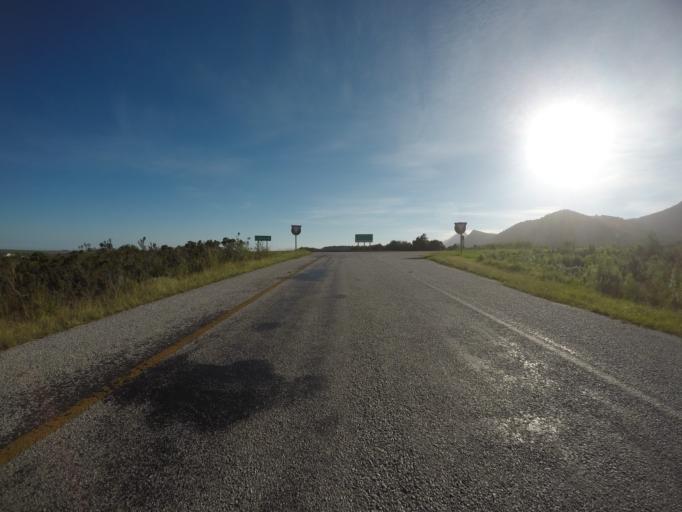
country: ZA
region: Eastern Cape
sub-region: Cacadu District Municipality
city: Kareedouw
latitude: -33.9997
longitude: 24.2359
